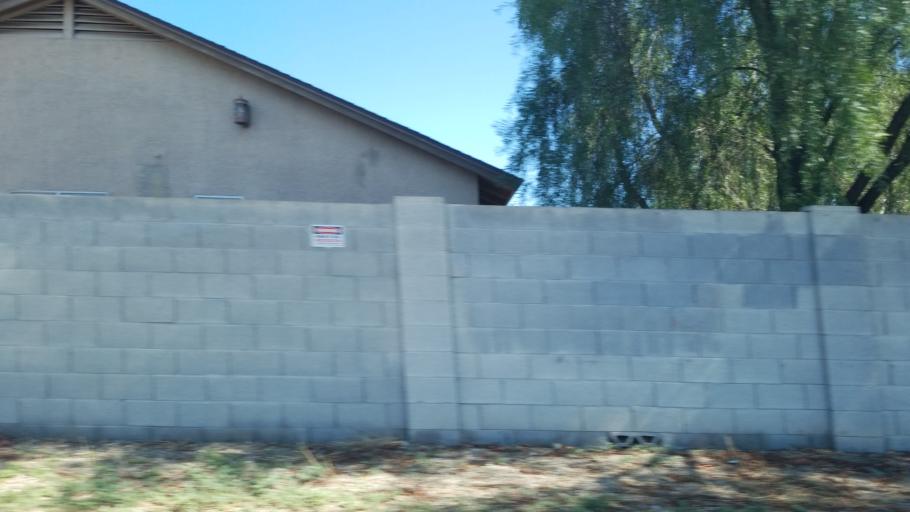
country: US
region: Arizona
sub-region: Maricopa County
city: Glendale
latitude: 33.5171
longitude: -112.2204
